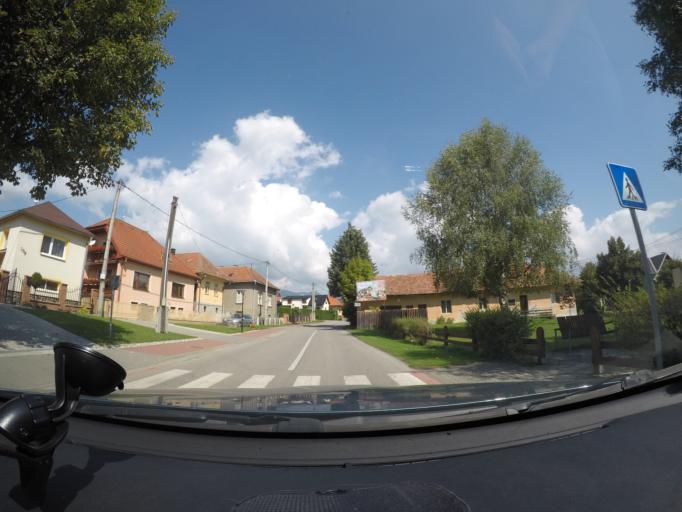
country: SK
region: Zilinsky
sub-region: Okres Liptovsky Mikulas
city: Liptovsky Mikulas
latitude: 49.1200
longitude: 19.6117
